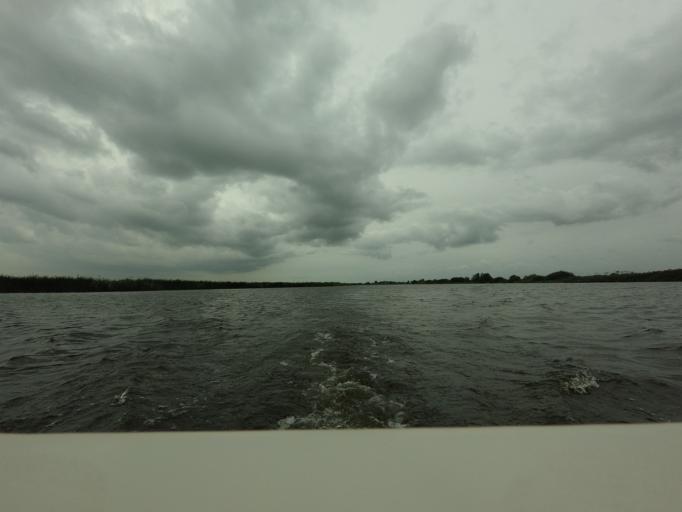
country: NL
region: Friesland
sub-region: Gemeente Boarnsterhim
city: Aldeboarn
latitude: 53.0954
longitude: 5.9344
